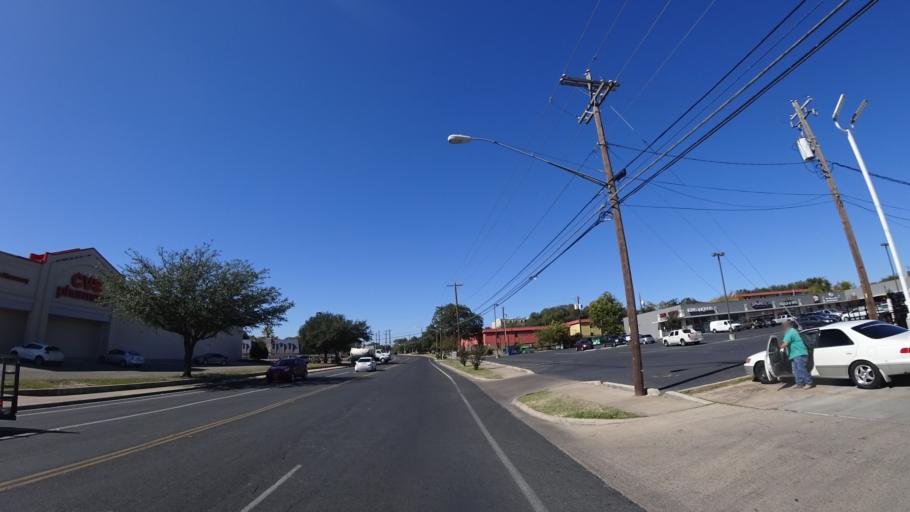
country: US
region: Texas
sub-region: Travis County
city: Austin
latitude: 30.3259
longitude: -97.7400
